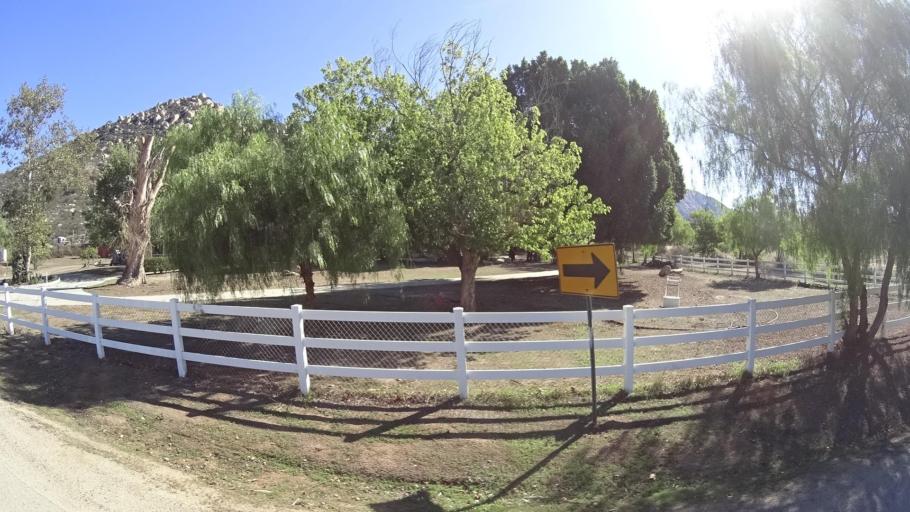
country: US
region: California
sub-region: San Diego County
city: Jamul
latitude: 32.7188
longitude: -116.8034
